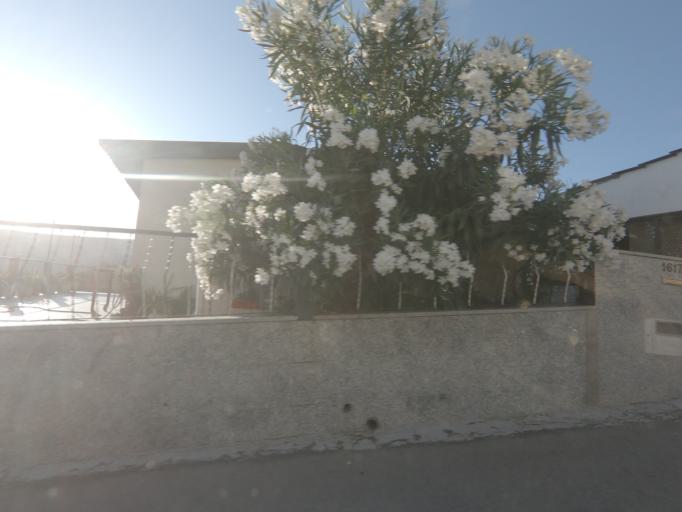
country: PT
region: Vila Real
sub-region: Peso da Regua
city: Godim
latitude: 41.1916
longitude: -7.8265
